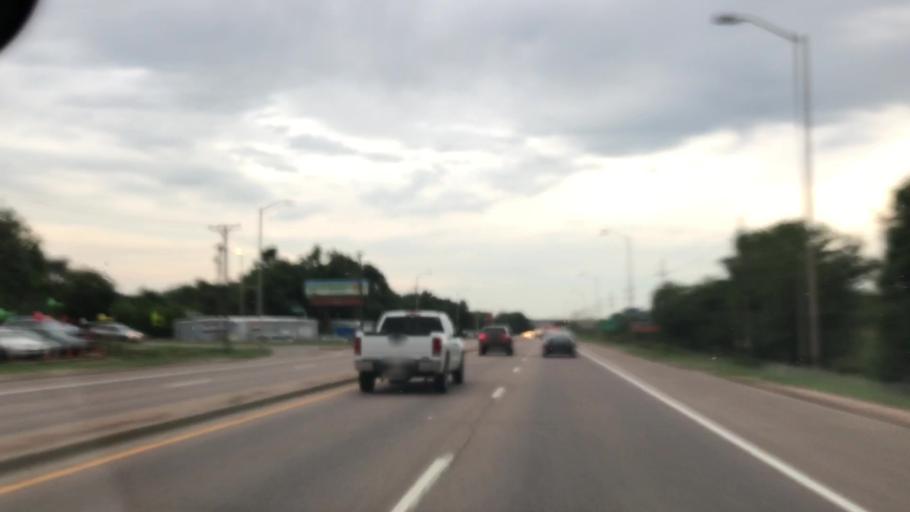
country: US
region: Colorado
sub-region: El Paso County
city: Colorado Springs
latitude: 38.8358
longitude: -104.8500
